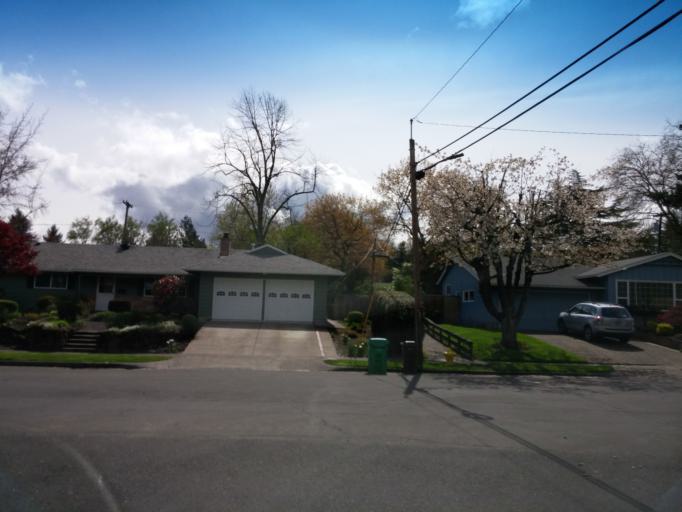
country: US
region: Oregon
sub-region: Washington County
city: Cedar Hills
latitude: 45.5104
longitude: -122.7979
